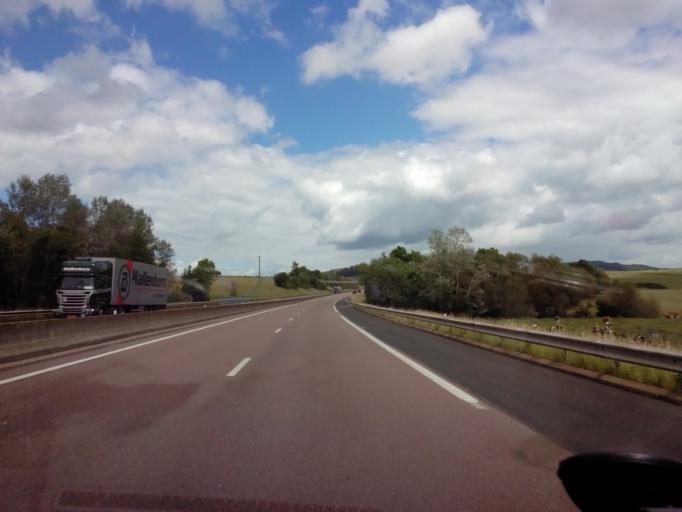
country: FR
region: Lorraine
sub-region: Departement des Vosges
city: Chatenois
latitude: 48.3490
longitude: 5.8572
